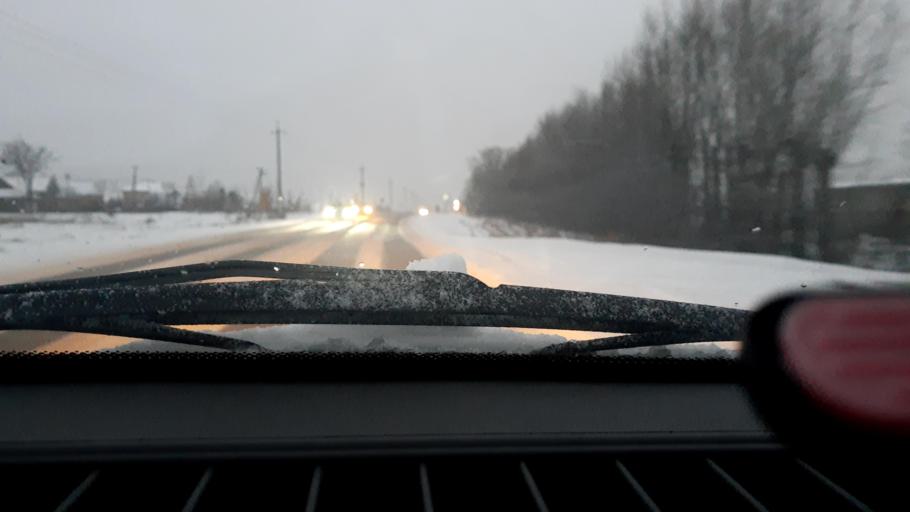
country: RU
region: Bashkortostan
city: Mikhaylovka
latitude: 54.8252
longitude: 55.8901
